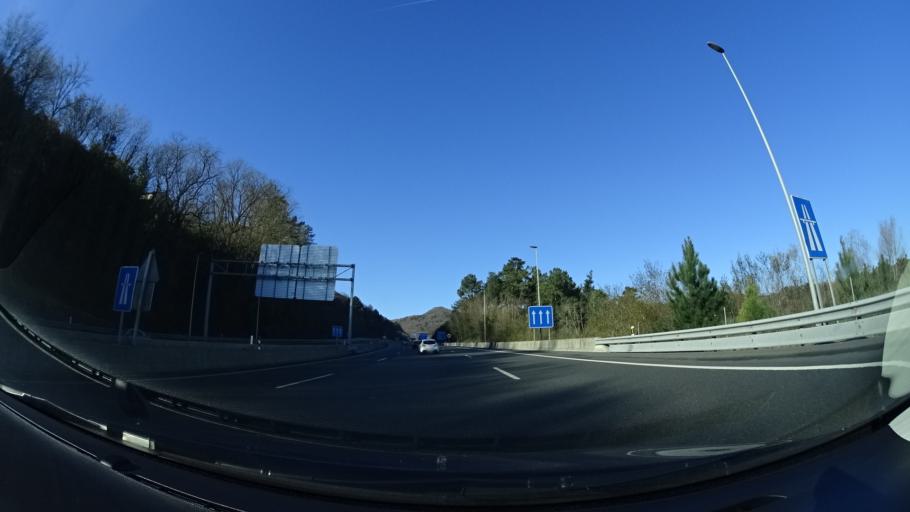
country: ES
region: Basque Country
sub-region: Provincia de Guipuzcoa
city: Usurbil
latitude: 43.2930
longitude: -2.0393
